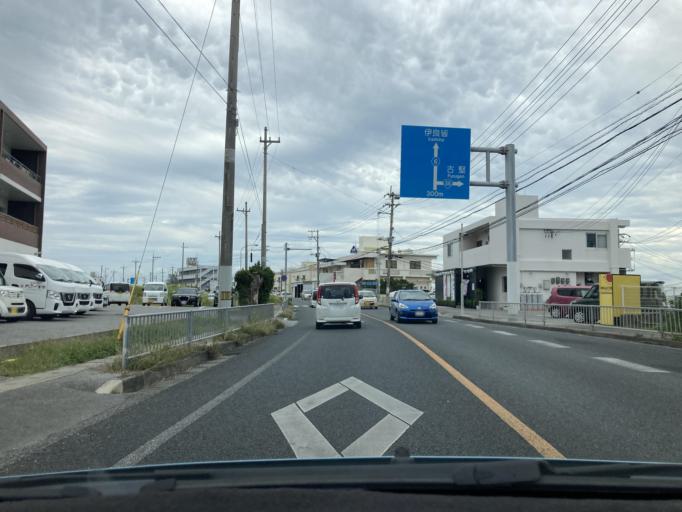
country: JP
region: Okinawa
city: Okinawa
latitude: 26.3833
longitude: 127.7424
